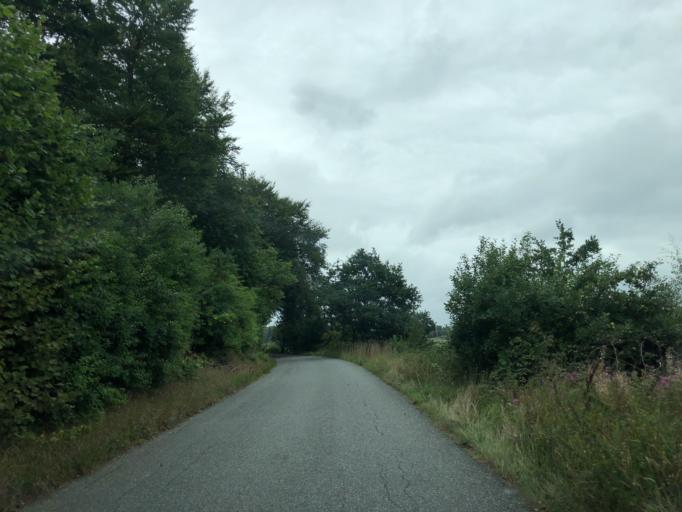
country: DK
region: Central Jutland
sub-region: Herning Kommune
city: Lind
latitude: 56.0795
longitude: 8.9604
